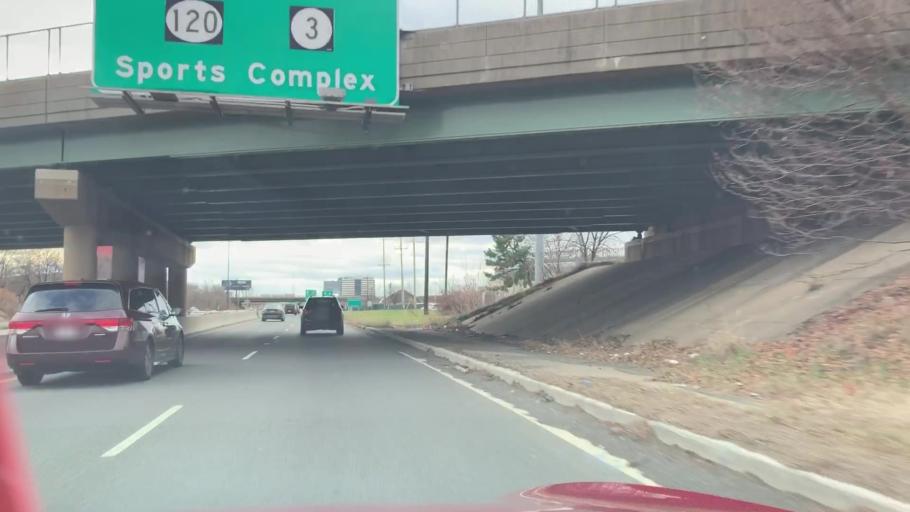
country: US
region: New Jersey
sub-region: Hudson County
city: Secaucus
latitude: 40.8172
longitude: -74.0666
